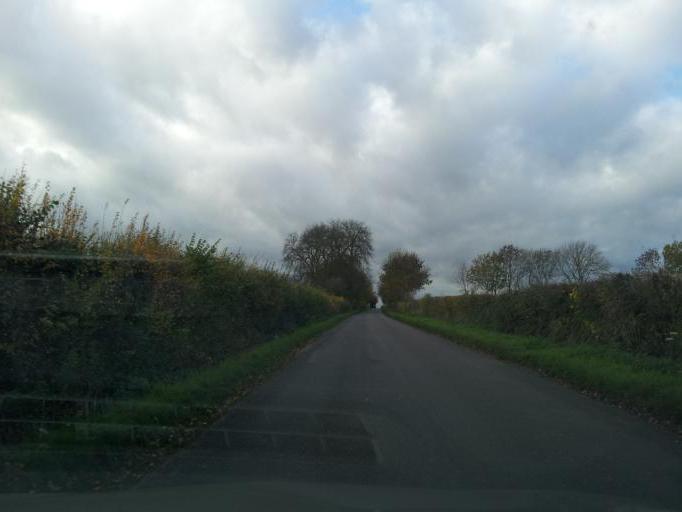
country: GB
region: England
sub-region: Lincolnshire
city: Long Bennington
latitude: 52.9837
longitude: -0.7940
